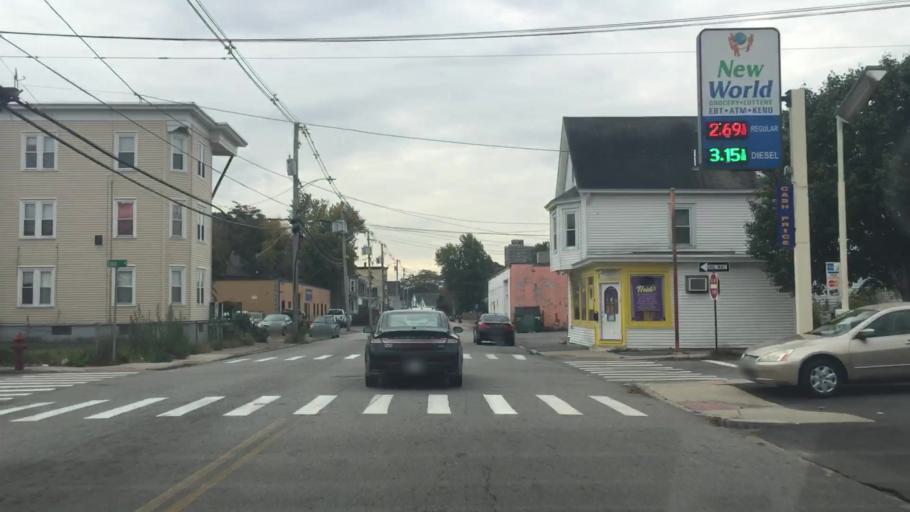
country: US
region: Massachusetts
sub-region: Middlesex County
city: Dracut
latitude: 42.6564
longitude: -71.3128
